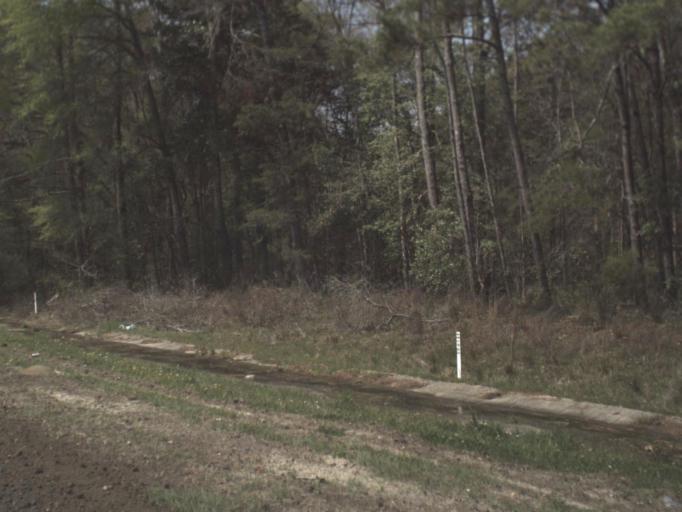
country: US
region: Florida
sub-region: Gadsden County
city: Midway
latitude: 30.5532
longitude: -84.5070
